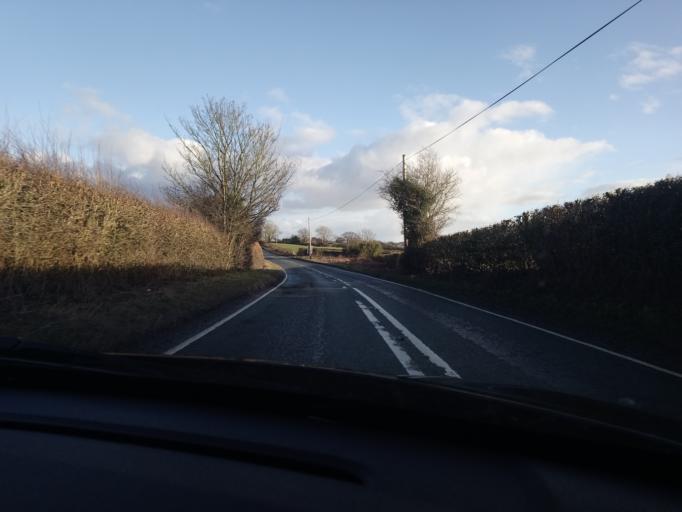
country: GB
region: England
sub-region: Shropshire
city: Whittington
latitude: 52.9256
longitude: -2.9830
